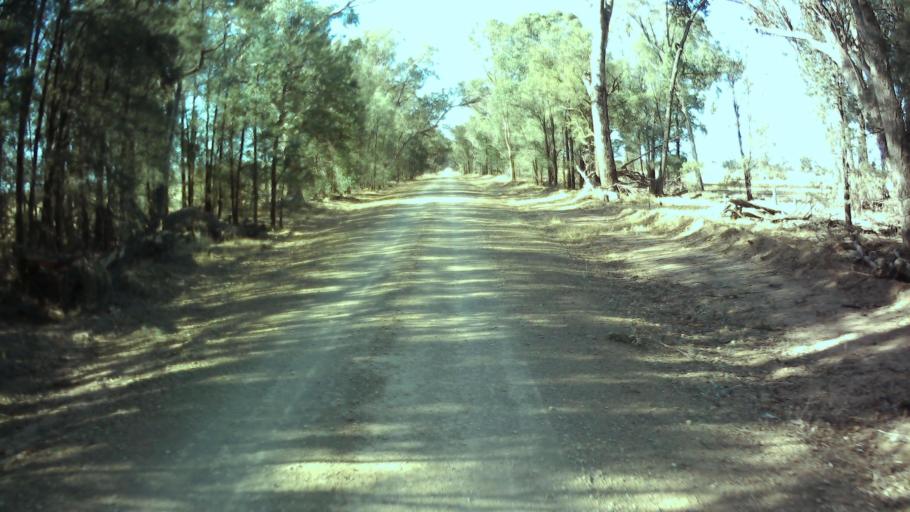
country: AU
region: New South Wales
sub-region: Weddin
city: Grenfell
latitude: -33.8197
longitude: 147.8756
